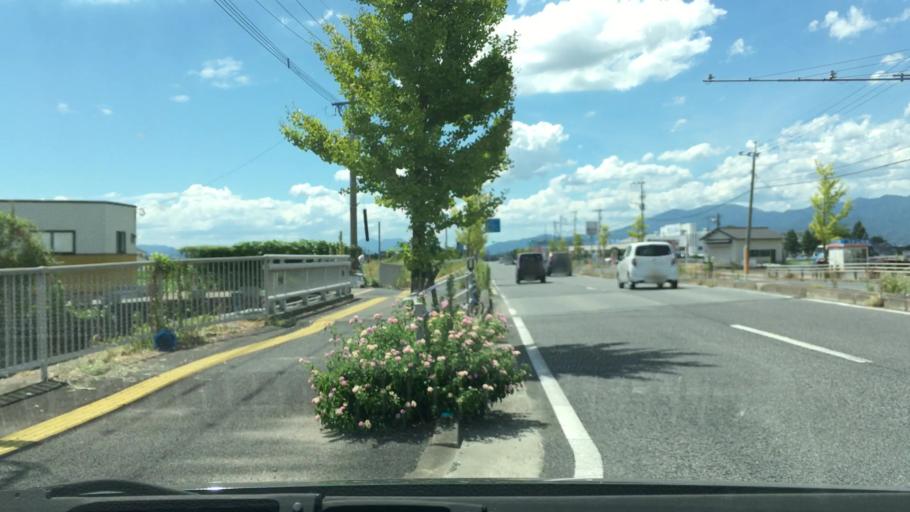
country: JP
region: Saga Prefecture
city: Saga-shi
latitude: 33.2739
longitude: 130.3324
